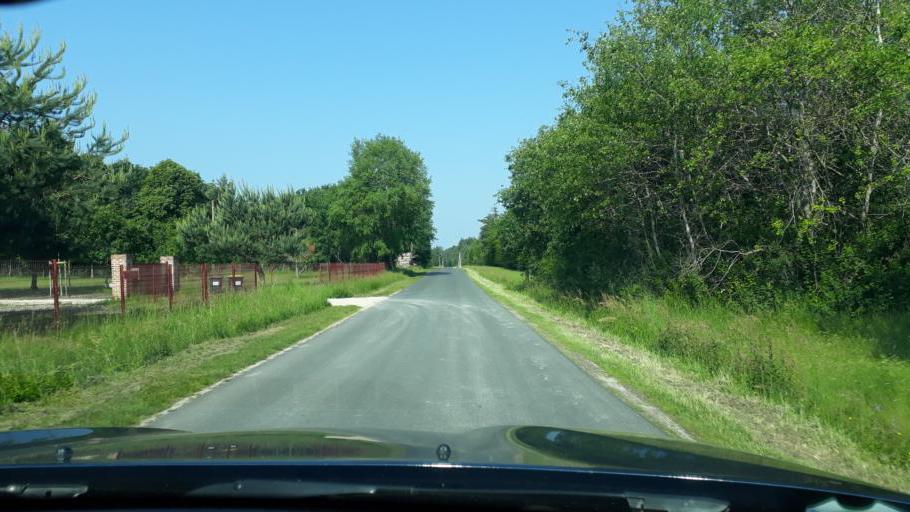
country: FR
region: Centre
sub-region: Departement du Loiret
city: Ligny-le-Ribault
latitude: 47.6217
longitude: 1.7443
